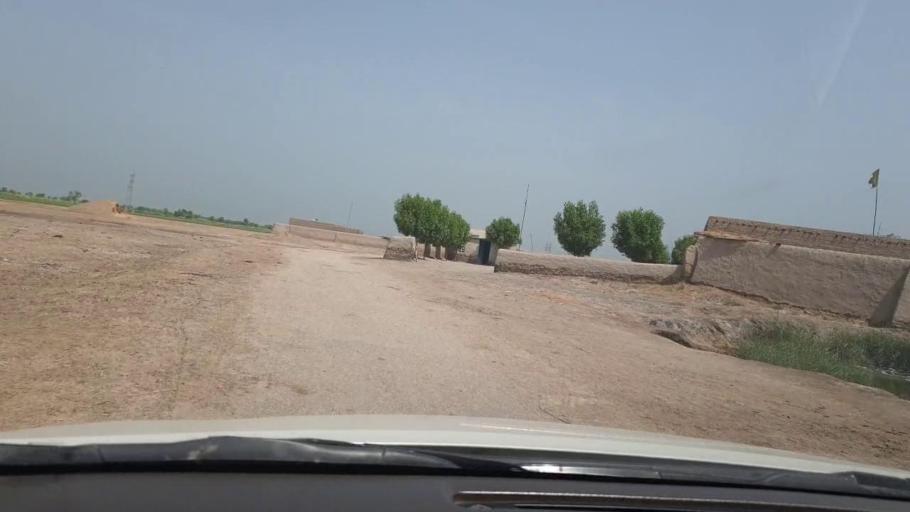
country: PK
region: Sindh
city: Shikarpur
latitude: 27.9981
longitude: 68.6234
